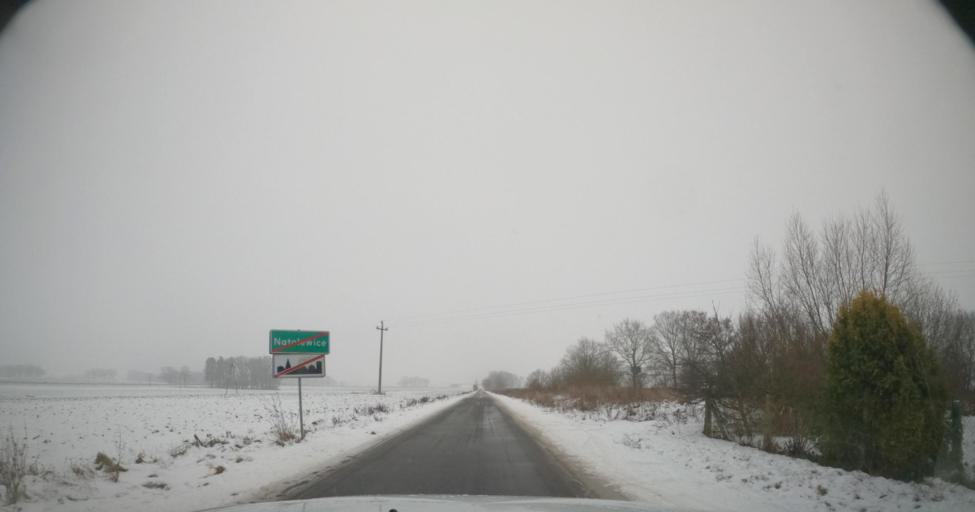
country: PL
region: West Pomeranian Voivodeship
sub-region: Powiat gryficki
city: Brojce
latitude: 53.8998
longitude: 15.3760
